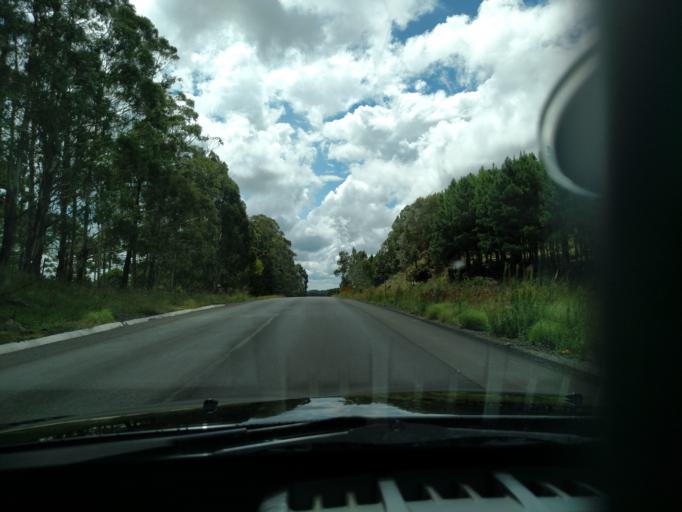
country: BR
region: Santa Catarina
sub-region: Lages
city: Lages
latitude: -27.9811
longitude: -50.0921
